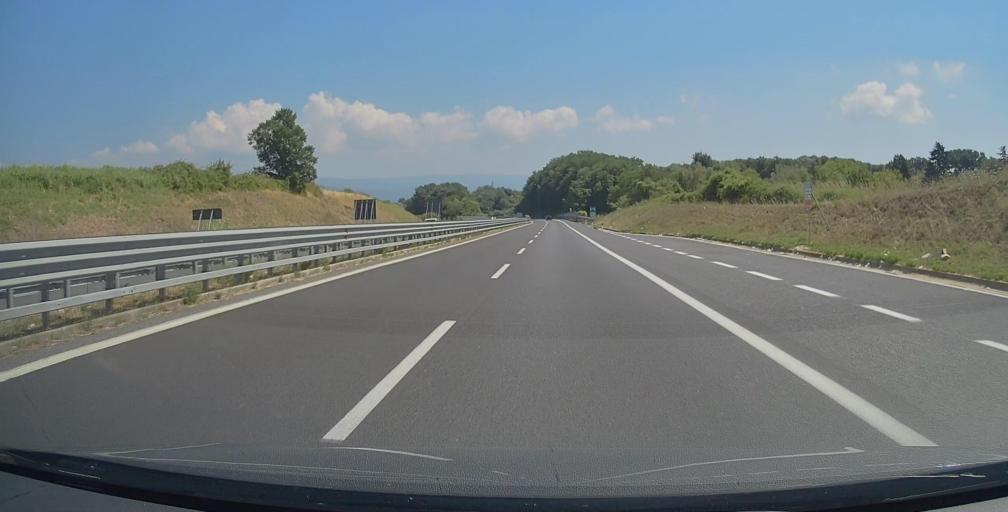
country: IT
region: Calabria
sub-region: Provincia di Vibo-Valentia
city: Sant'Onofrio
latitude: 38.6934
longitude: 16.1567
